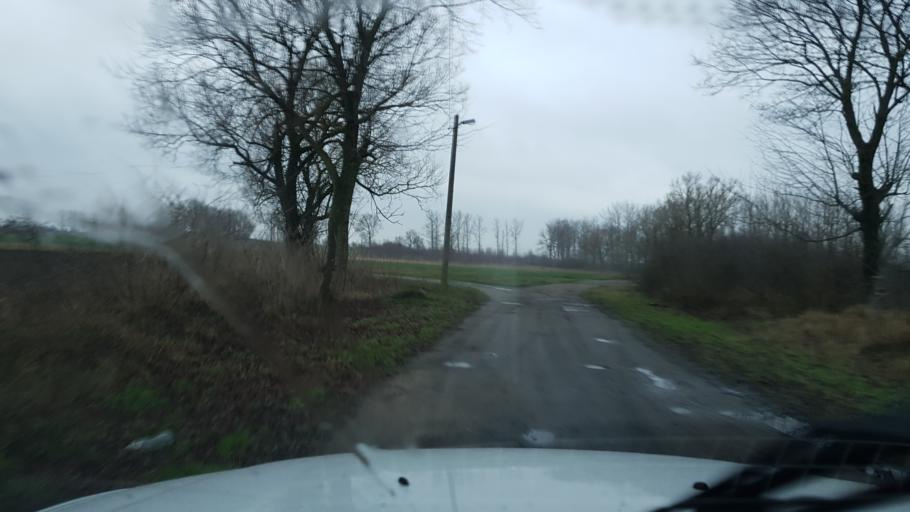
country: PL
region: West Pomeranian Voivodeship
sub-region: Powiat gryficki
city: Brojce
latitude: 53.9885
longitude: 15.3124
